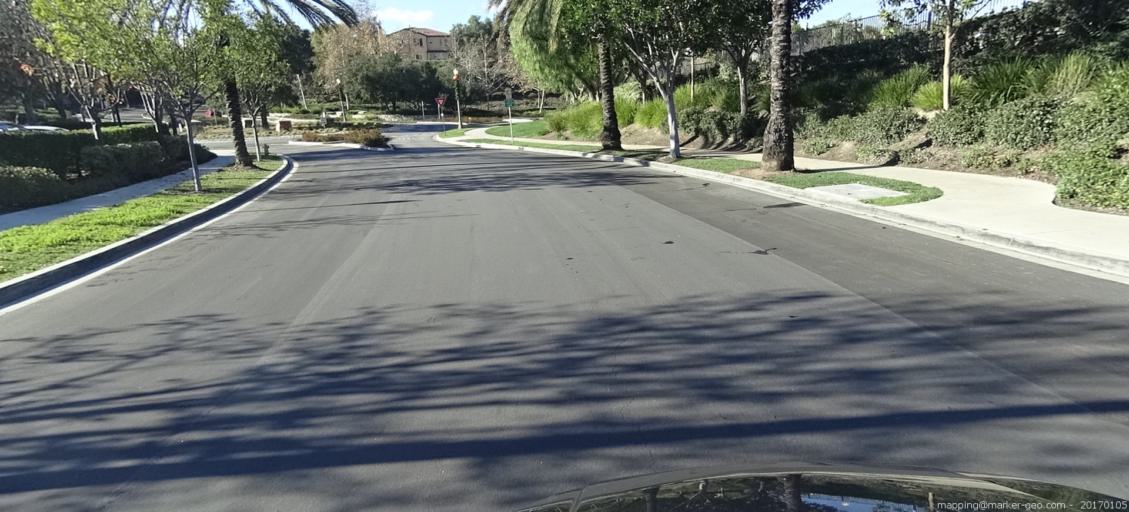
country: US
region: California
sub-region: Orange County
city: Ladera Ranch
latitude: 33.5518
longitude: -117.6376
